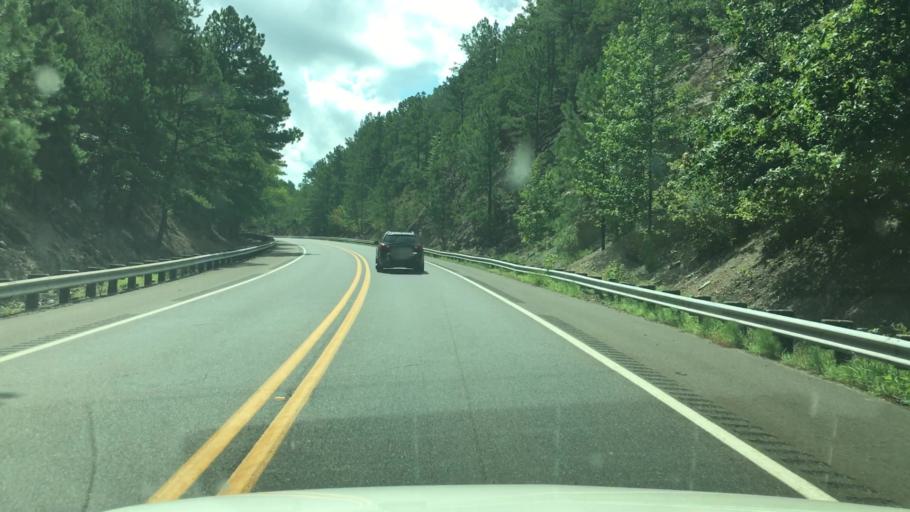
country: US
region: Arkansas
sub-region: Clark County
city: Arkadelphia
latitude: 34.2316
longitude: -93.0990
